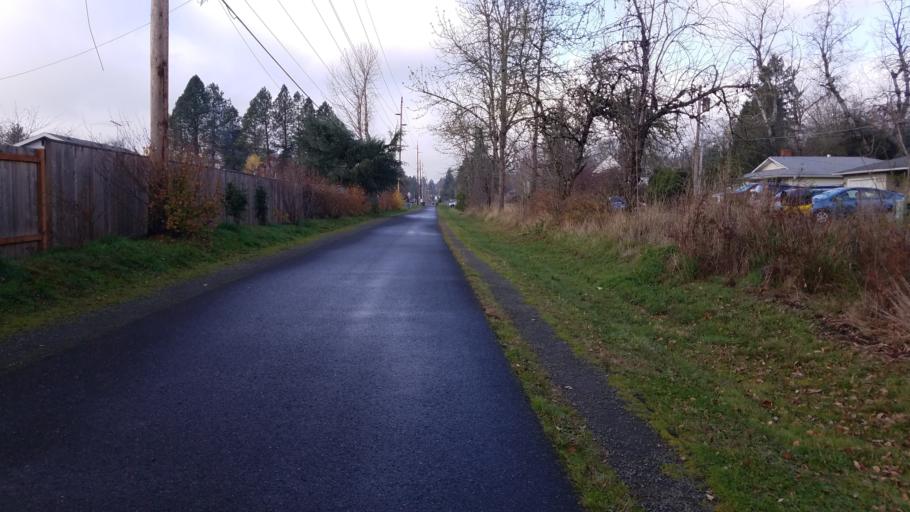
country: US
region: Oregon
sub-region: Clackamas County
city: Oak Grove
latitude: 45.4051
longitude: -122.6327
